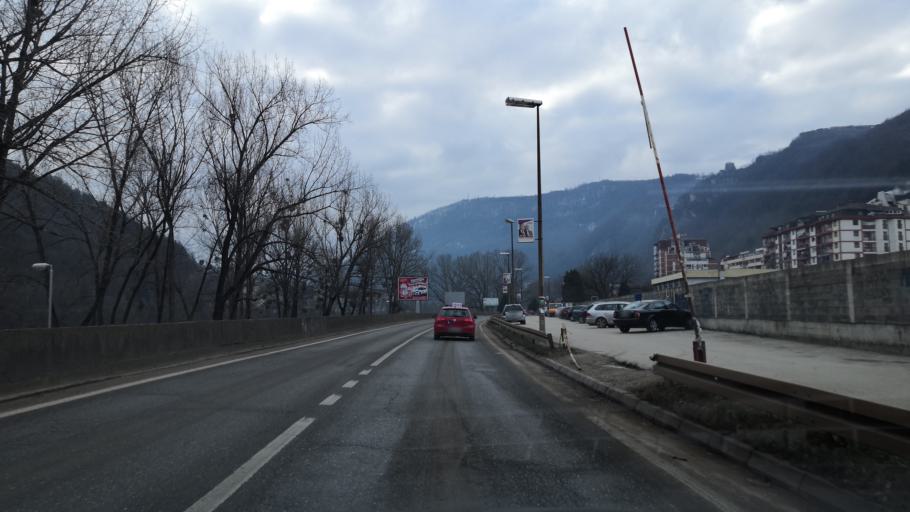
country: BA
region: Republika Srpska
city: Zvornik
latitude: 44.3838
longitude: 19.1054
